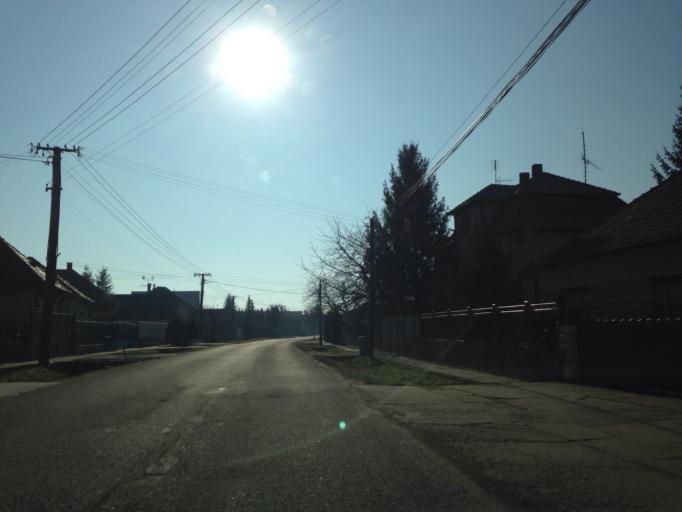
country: SK
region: Nitriansky
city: Svodin
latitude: 47.9252
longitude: 18.4028
